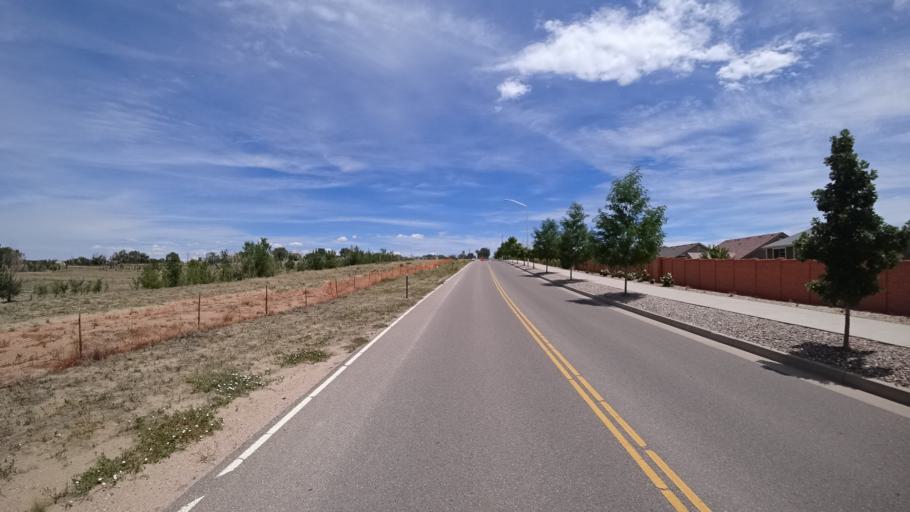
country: US
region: Colorado
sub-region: El Paso County
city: Fountain
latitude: 38.6940
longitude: -104.6762
